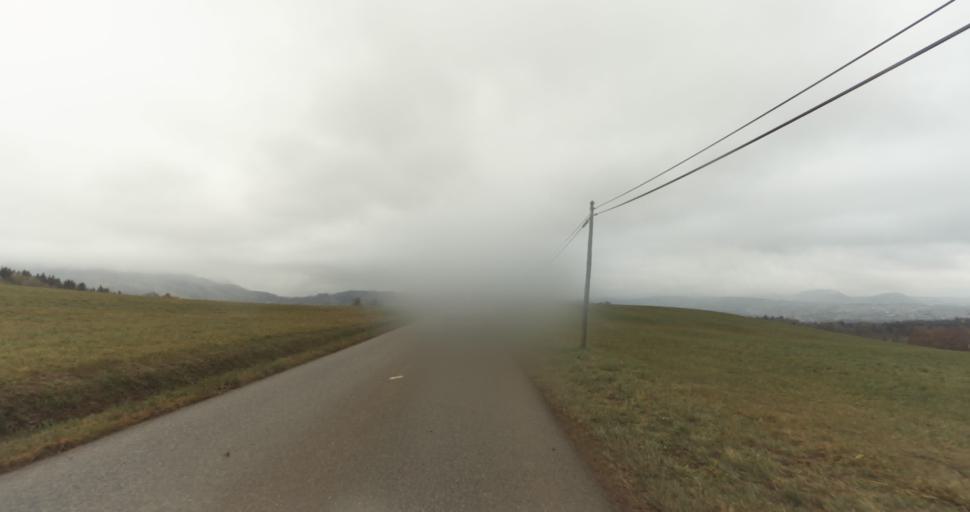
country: FR
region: Rhone-Alpes
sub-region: Departement de la Haute-Savoie
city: Thorens-Glieres
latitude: 46.0124
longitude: 6.2395
